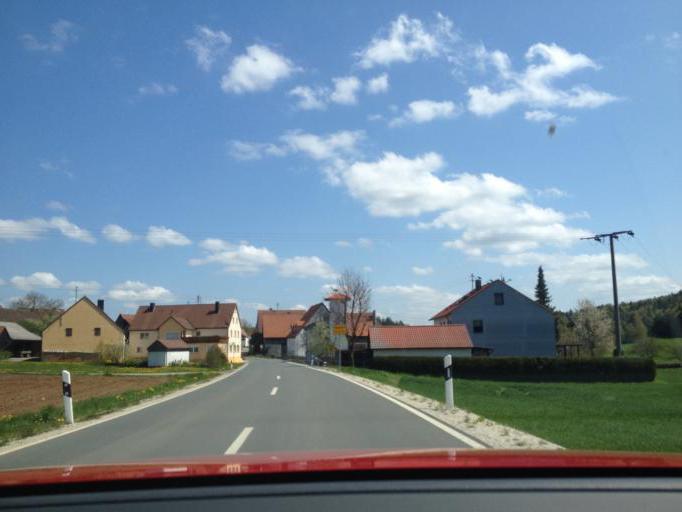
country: DE
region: Bavaria
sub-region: Upper Franconia
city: Obertrubach
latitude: 49.6667
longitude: 11.4026
